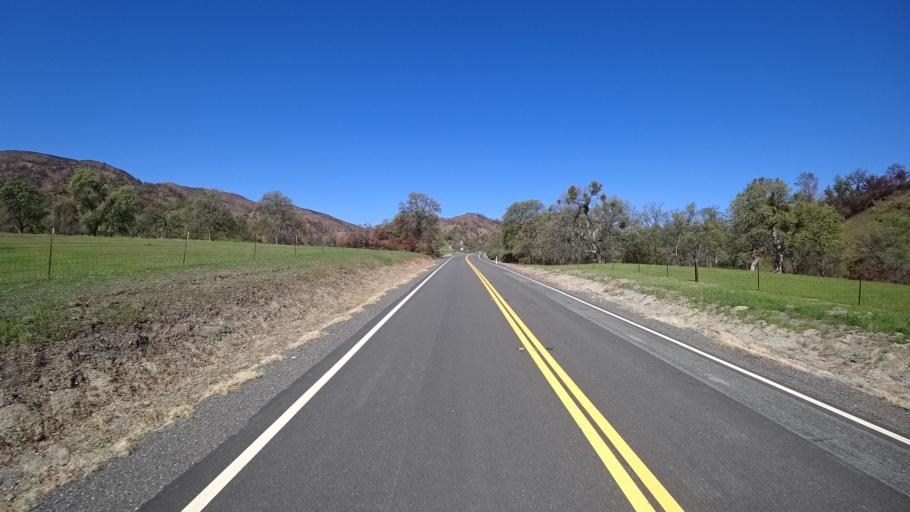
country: US
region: California
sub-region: Glenn County
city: Orland
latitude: 39.6549
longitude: -122.5880
